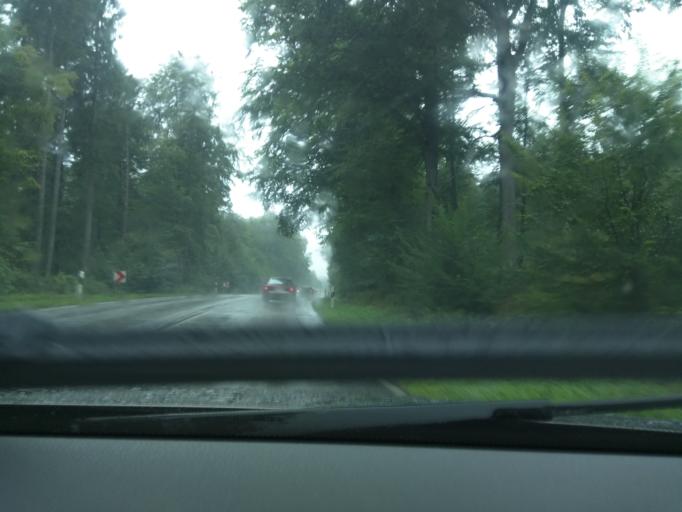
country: DE
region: Schleswig-Holstein
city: Brunstorf
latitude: 53.5161
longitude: 10.4541
